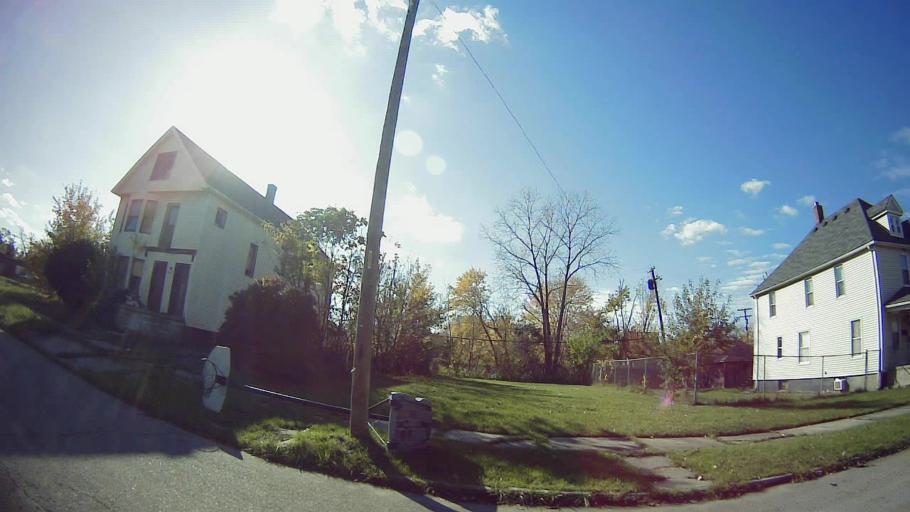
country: US
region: Michigan
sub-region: Wayne County
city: Detroit
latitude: 42.3446
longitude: -83.1007
